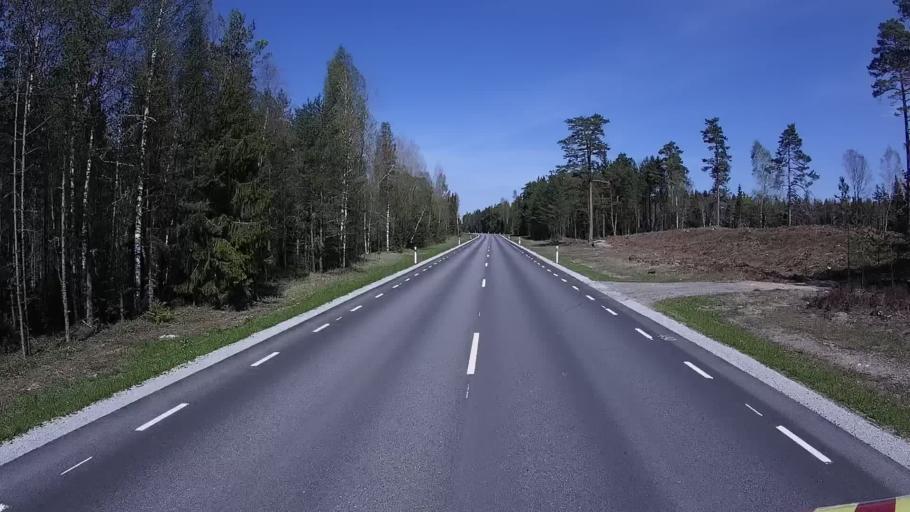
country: EE
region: Harju
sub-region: Nissi vald
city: Turba
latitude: 59.1349
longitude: 24.0741
